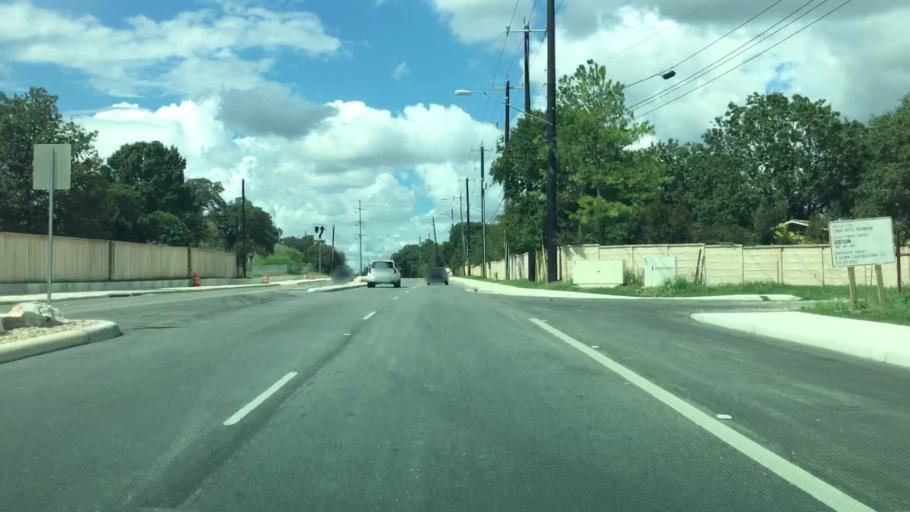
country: US
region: Texas
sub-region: Bexar County
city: Hollywood Park
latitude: 29.6055
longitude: -98.4436
